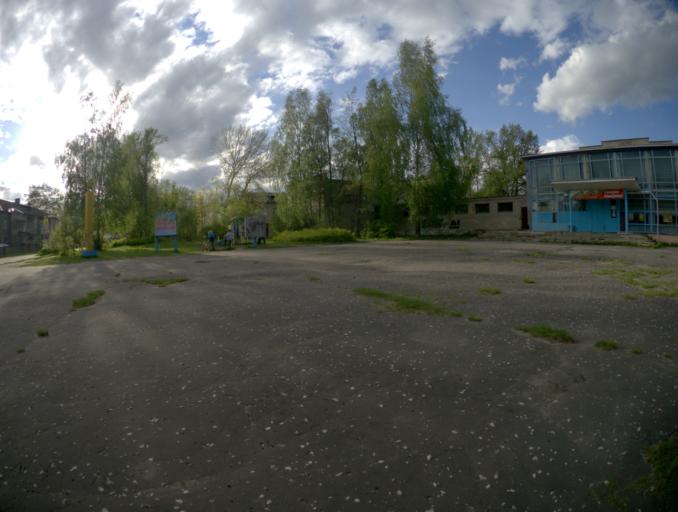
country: RU
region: Vladimir
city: Gusevskiy
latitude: 55.6599
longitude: 40.5632
